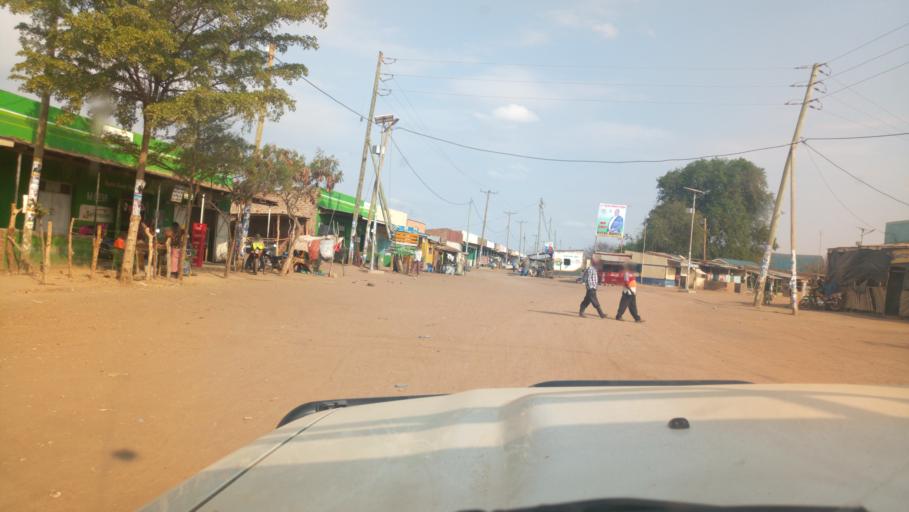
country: KE
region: Makueni
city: Wote
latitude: -1.6763
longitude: 37.9221
